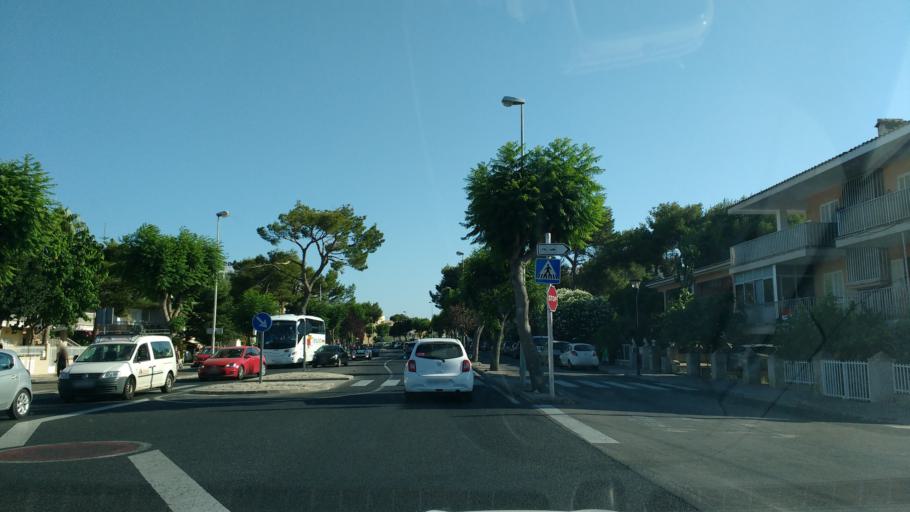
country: ES
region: Balearic Islands
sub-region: Illes Balears
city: Port d'Alcudia
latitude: 39.8182
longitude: 3.1140
